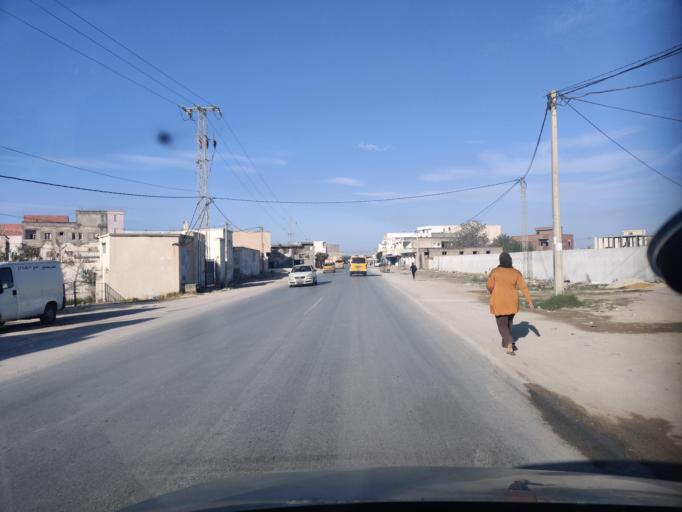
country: TN
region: Ariana
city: Ariana
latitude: 36.9562
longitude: 10.2148
